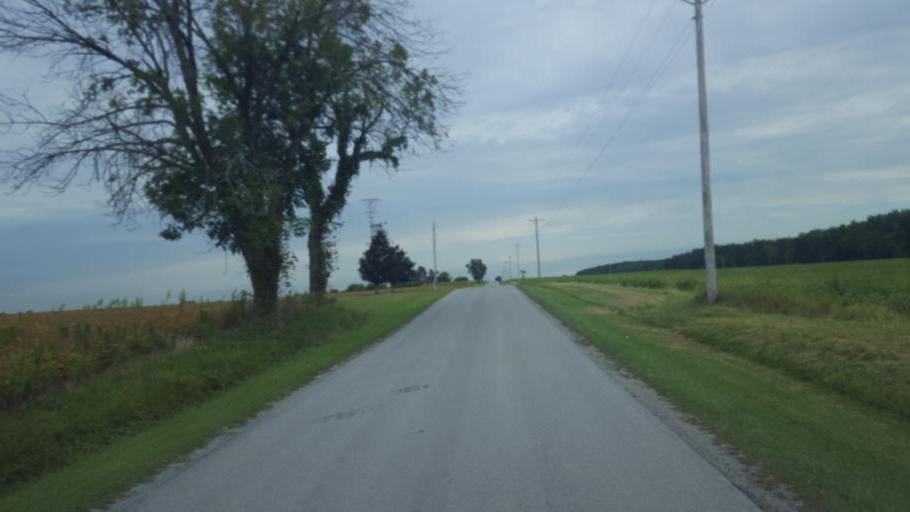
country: US
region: Ohio
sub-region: Wyandot County
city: Upper Sandusky
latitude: 40.7846
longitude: -83.1884
